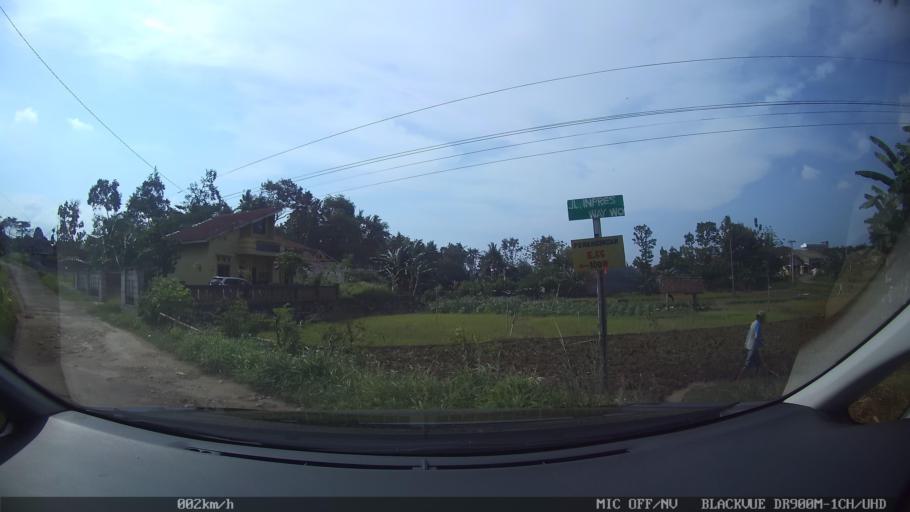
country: ID
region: Lampung
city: Kedaton
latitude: -5.3829
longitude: 105.2305
